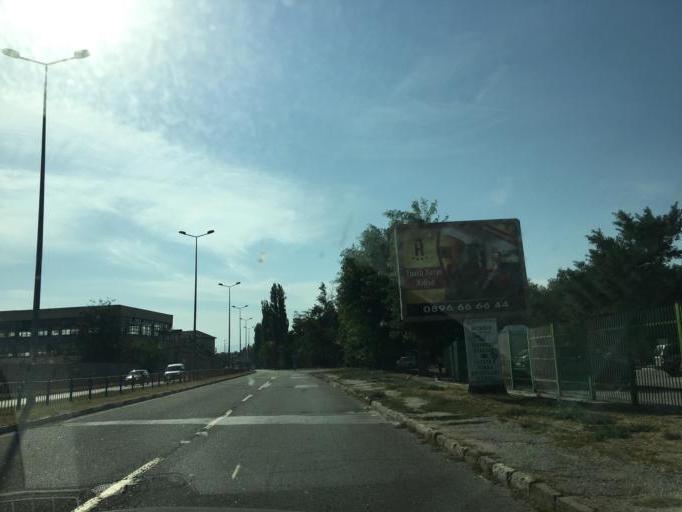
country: BG
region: Pazardzhik
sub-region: Obshtina Pazardzhik
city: Pazardzhik
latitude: 42.2113
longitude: 24.3235
